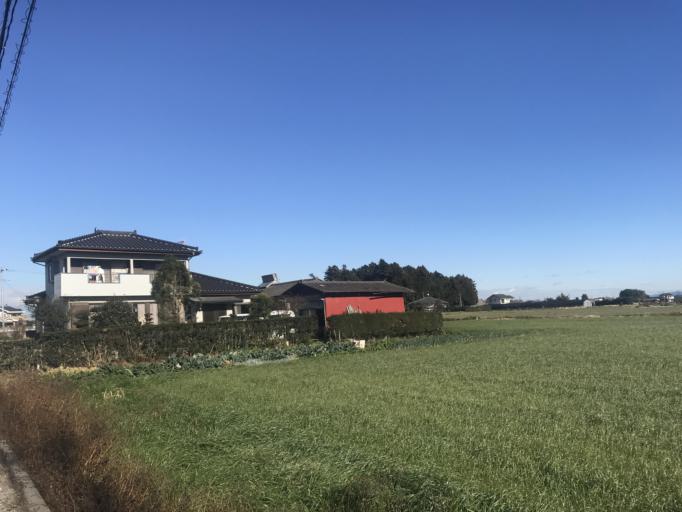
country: JP
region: Ibaraki
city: Yuki
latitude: 36.3635
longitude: 139.8768
